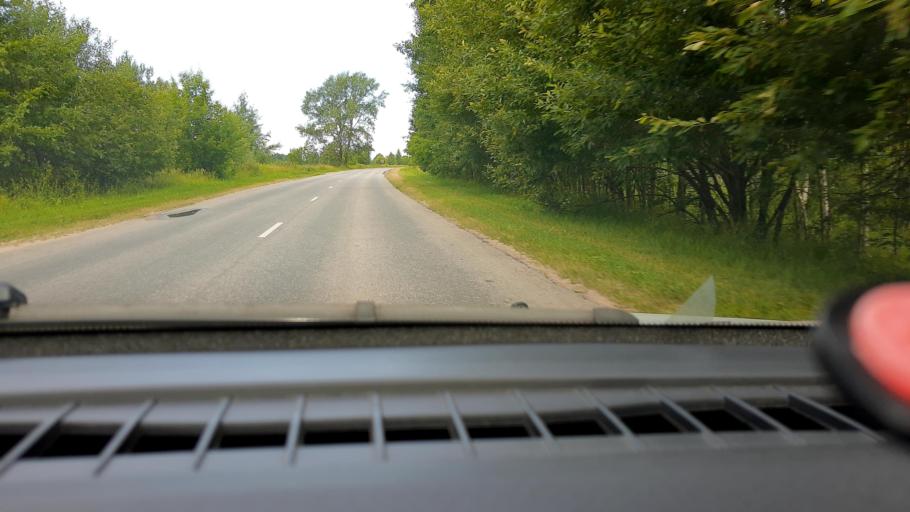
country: RU
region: Nizjnij Novgorod
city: Kstovo
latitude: 56.1503
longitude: 44.2962
